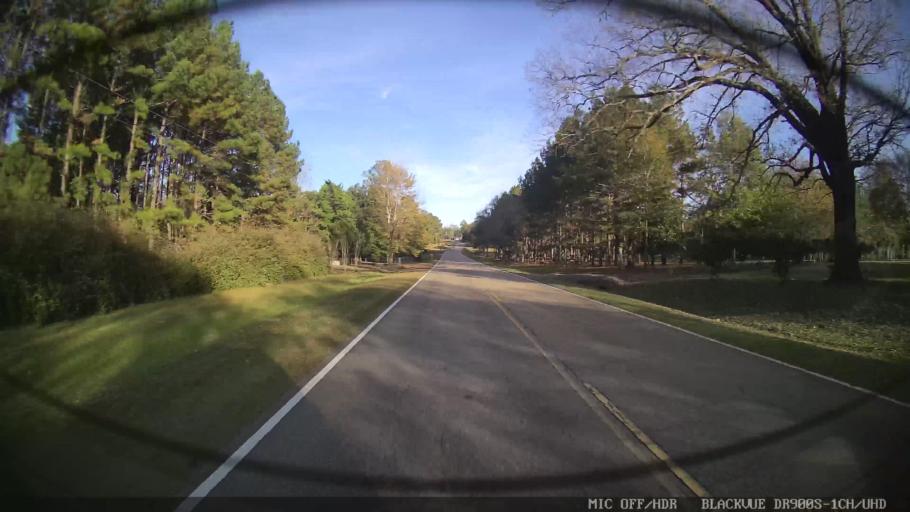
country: US
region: Mississippi
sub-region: Lamar County
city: Purvis
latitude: 31.1658
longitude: -89.3123
